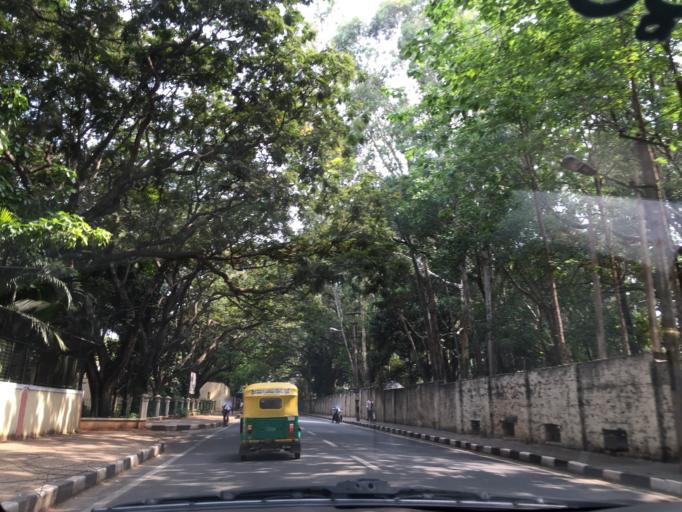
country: IN
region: Karnataka
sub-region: Bangalore Urban
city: Bangalore
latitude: 12.9855
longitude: 77.5931
